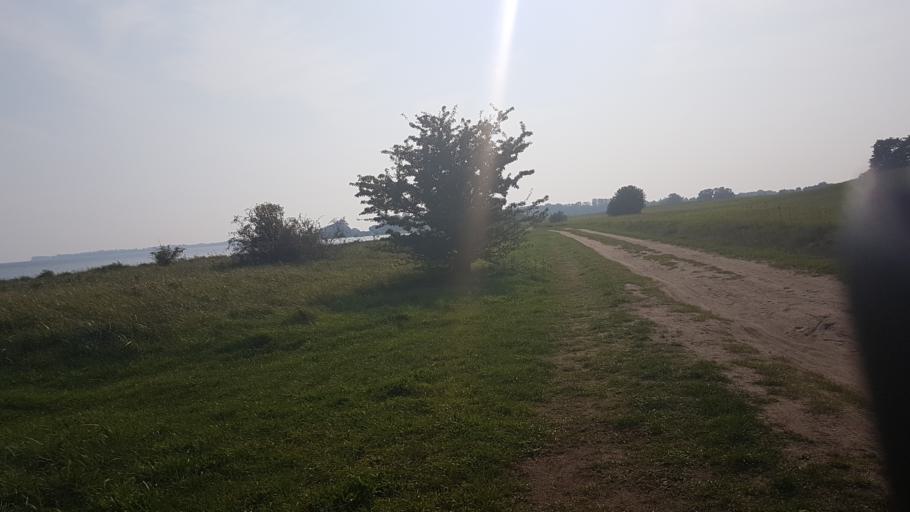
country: DE
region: Mecklenburg-Vorpommern
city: Garz
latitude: 54.3025
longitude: 13.4186
